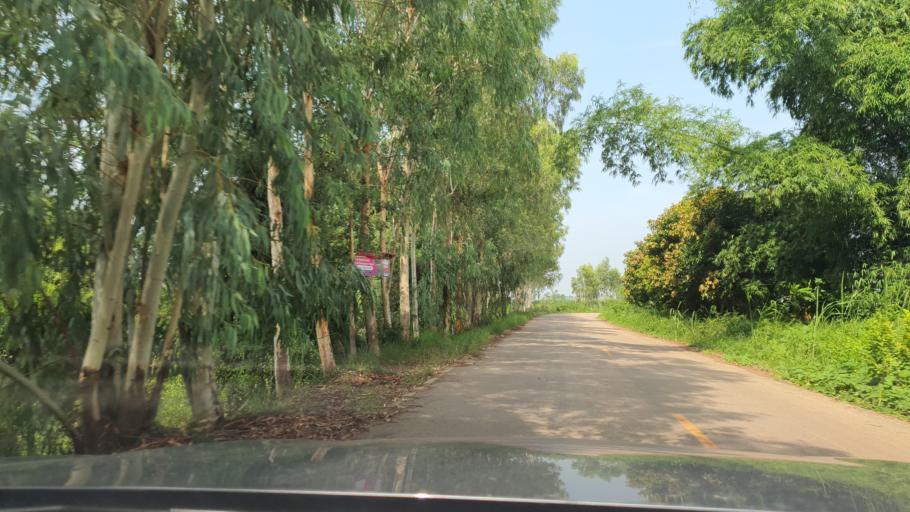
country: TH
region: Phitsanulok
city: Bang Rakam
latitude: 16.8020
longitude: 100.1184
